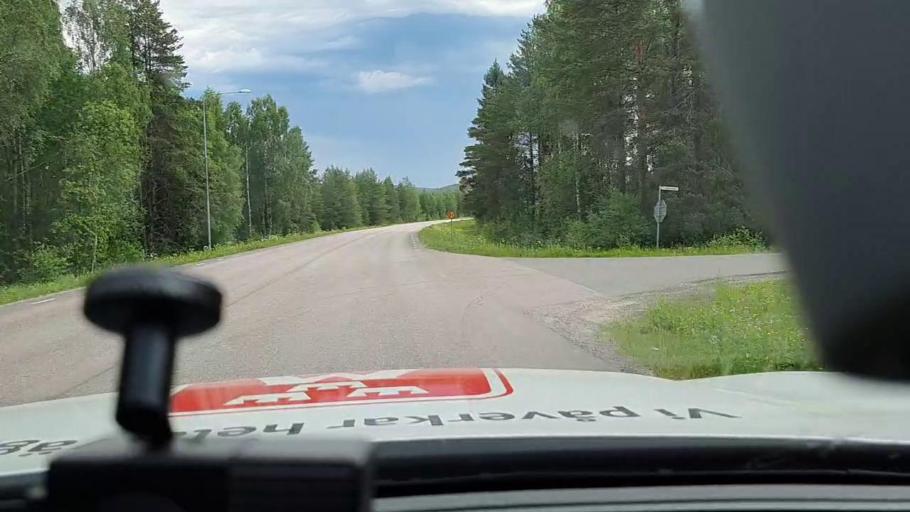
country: SE
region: Norrbotten
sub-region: Bodens Kommun
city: Boden
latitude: 65.8179
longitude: 21.5882
